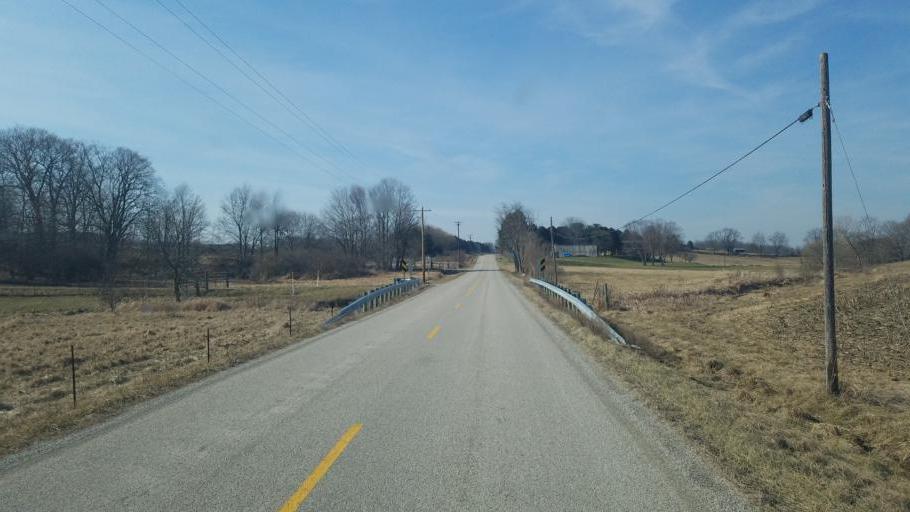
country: US
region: Ohio
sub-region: Ashland County
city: Ashland
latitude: 40.8058
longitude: -82.2528
